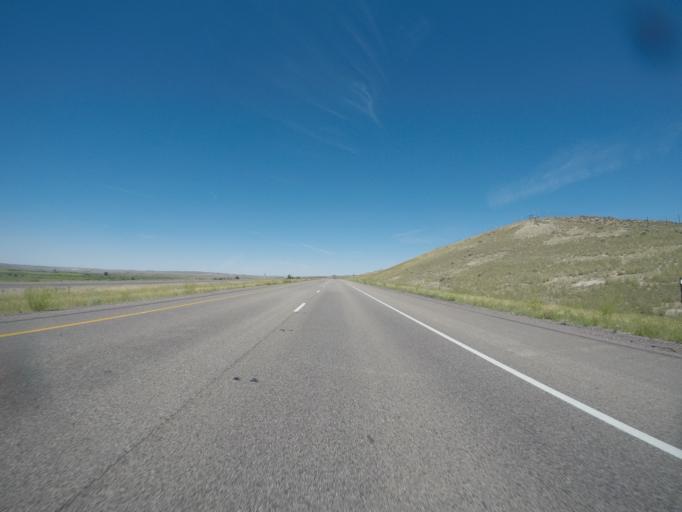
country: US
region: Wyoming
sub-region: Carbon County
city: Saratoga
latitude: 41.7405
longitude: -106.7590
